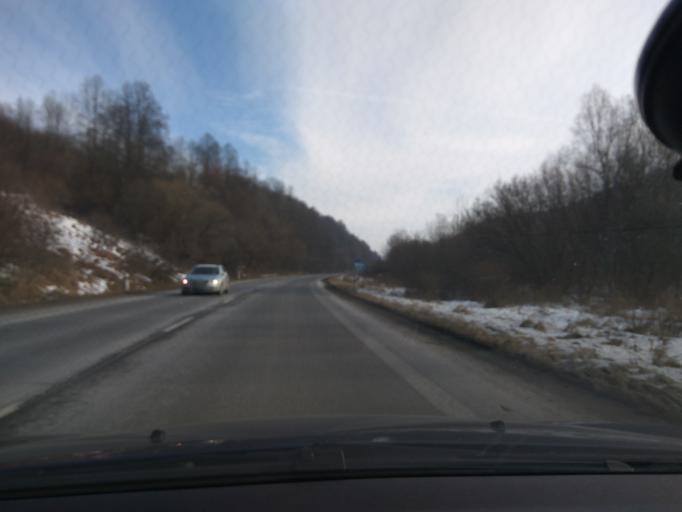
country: SK
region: Banskobystricky
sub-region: Okres Banska Bystrica
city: Brezno
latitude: 48.8117
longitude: 19.6039
